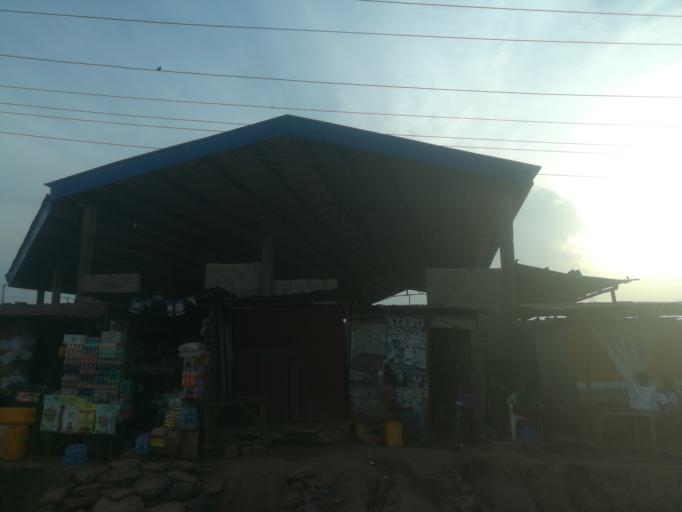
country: NG
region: Oyo
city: Moniya
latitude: 7.5336
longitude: 3.9074
